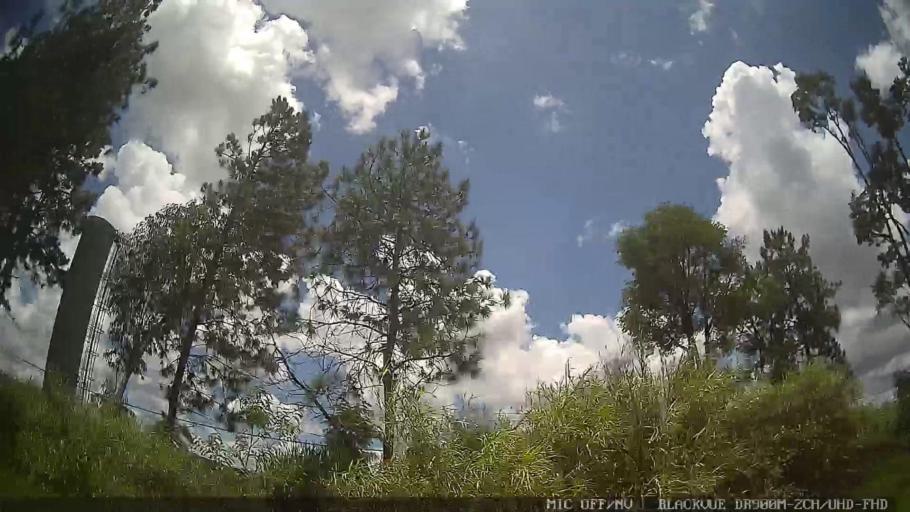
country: BR
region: Sao Paulo
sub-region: Serra Negra
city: Serra Negra
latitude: -22.6296
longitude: -46.7223
